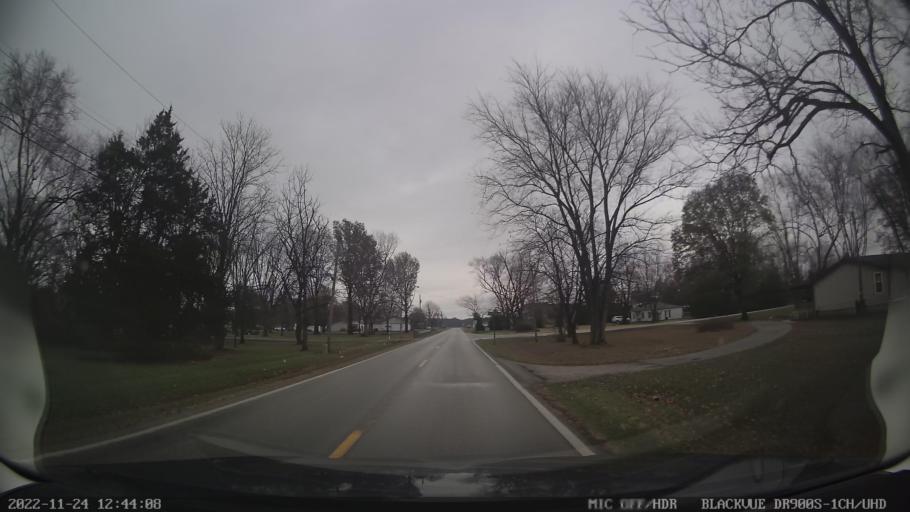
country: US
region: Illinois
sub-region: Macoupin County
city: Staunton
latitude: 38.9614
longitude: -89.7676
